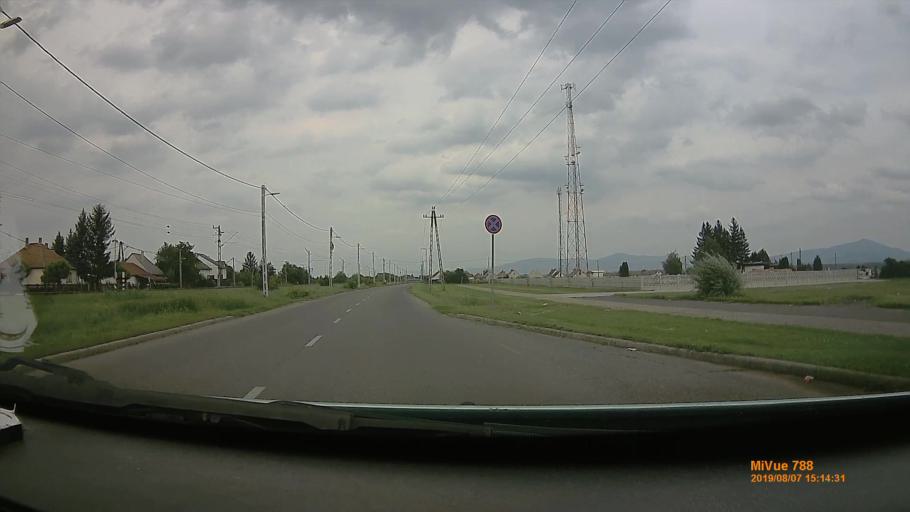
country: HU
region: Borsod-Abauj-Zemplen
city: Encs
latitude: 48.3322
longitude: 21.1233
